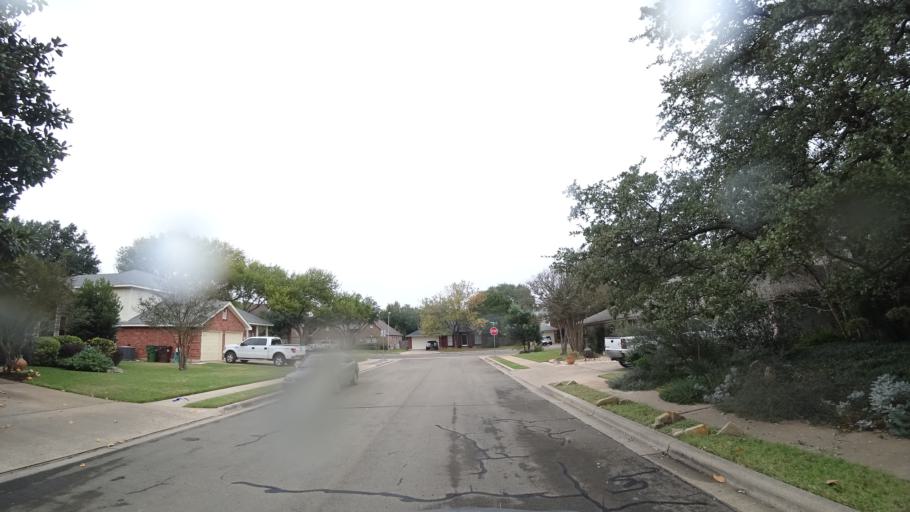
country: US
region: Texas
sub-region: Williamson County
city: Brushy Creek
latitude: 30.5168
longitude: -97.7121
